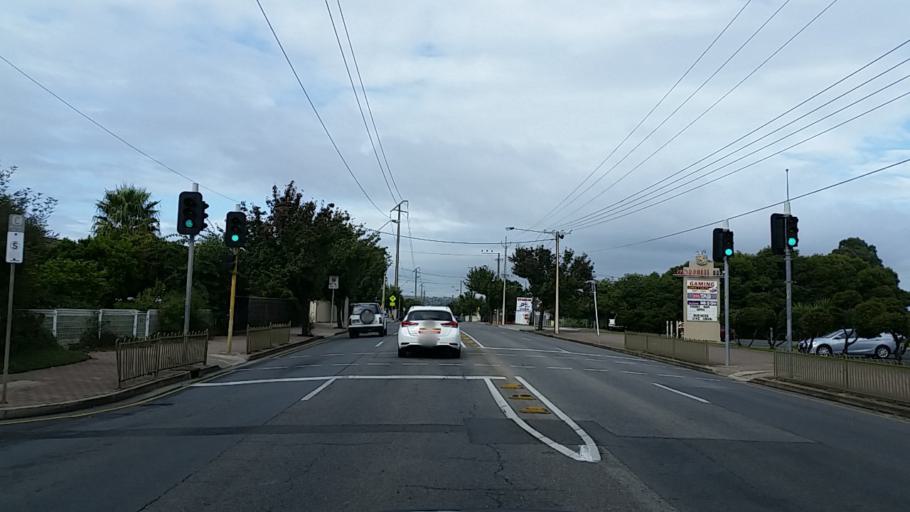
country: AU
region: South Australia
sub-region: Marion
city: Plympton Park
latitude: -34.9868
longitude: 138.5386
